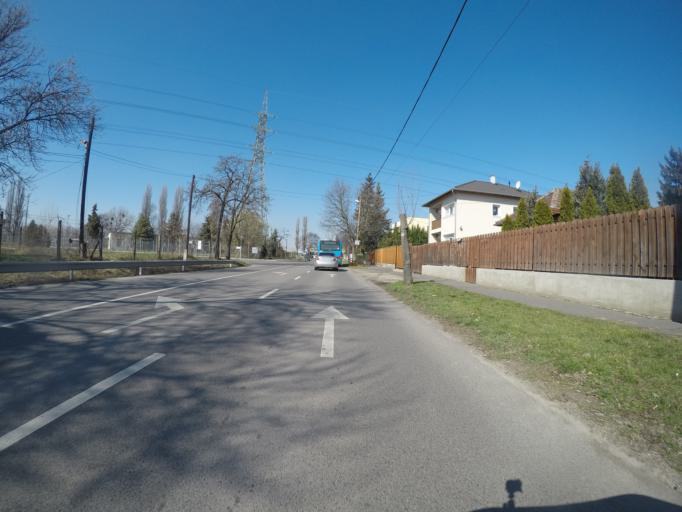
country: HU
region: Budapest
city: Budapest XIX. keruelet
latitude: 47.4355
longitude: 19.1529
